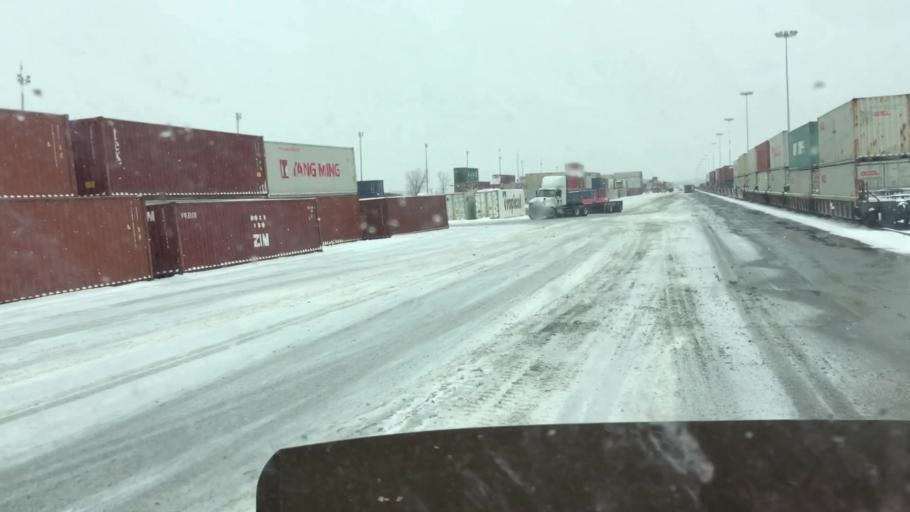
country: CA
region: Quebec
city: Cote-Saint-Luc
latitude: 45.4634
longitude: -73.6915
